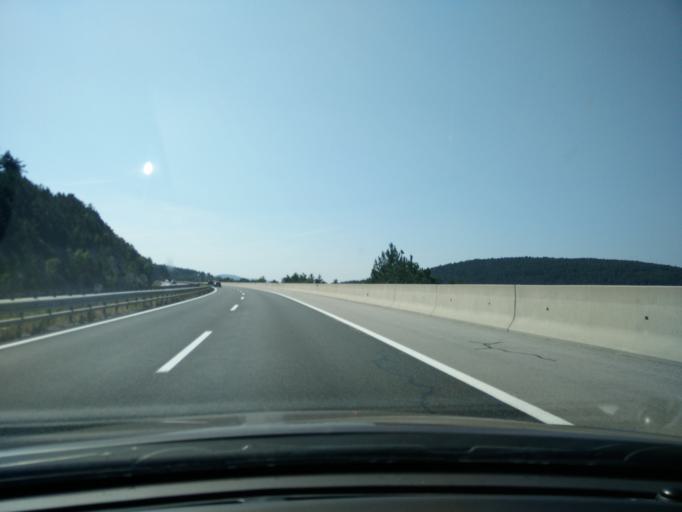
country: SI
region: Divaca
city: Divaca
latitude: 45.7146
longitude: 14.0021
